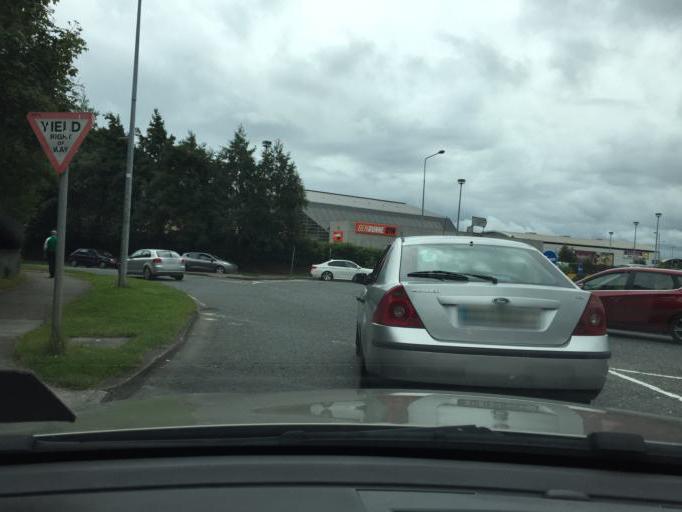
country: IE
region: Leinster
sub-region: Fingal County
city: Blanchardstown
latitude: 53.3931
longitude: -6.3852
